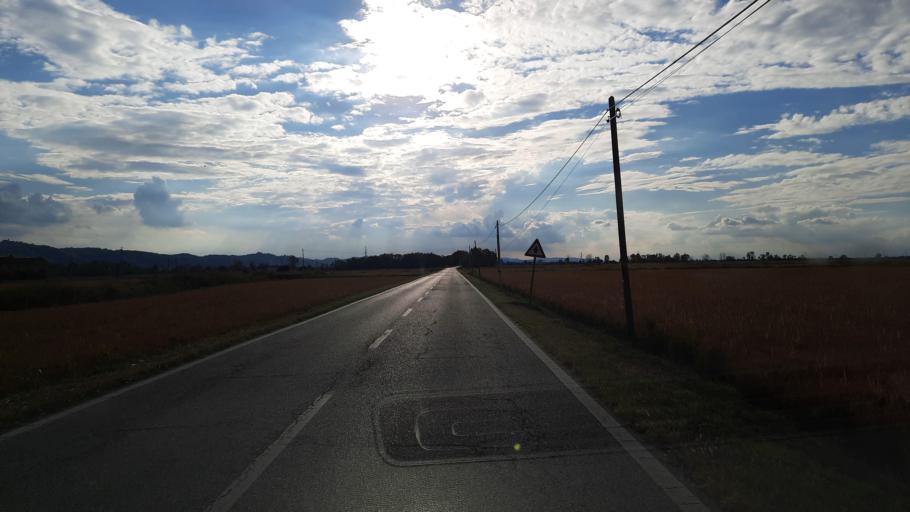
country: IT
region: Piedmont
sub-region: Provincia di Vercelli
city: Trino
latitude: 45.1938
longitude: 8.2665
